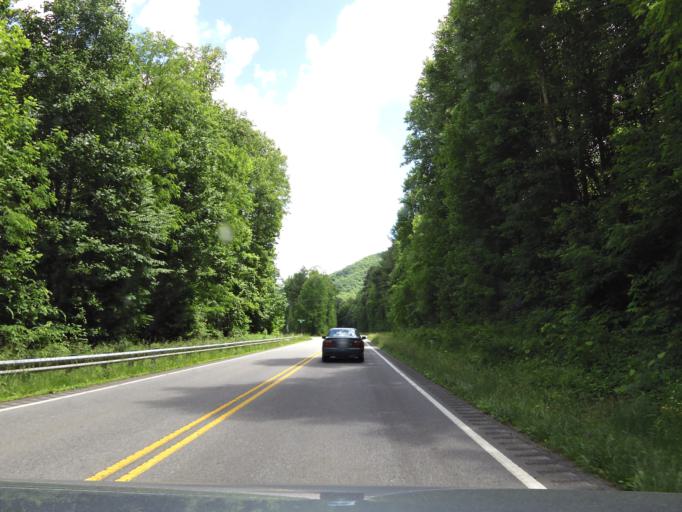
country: US
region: North Carolina
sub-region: Graham County
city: Robbinsville
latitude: 35.2714
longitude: -83.7235
